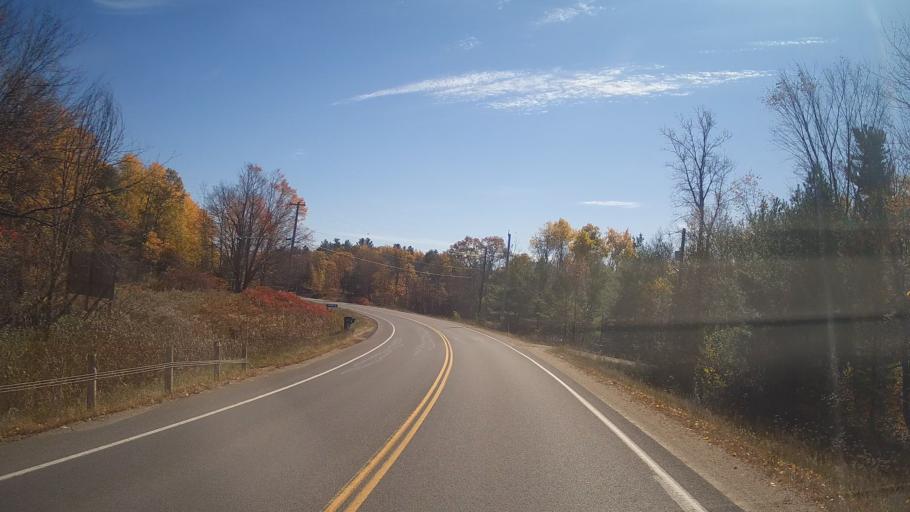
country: CA
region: Ontario
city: Perth
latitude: 44.7274
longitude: -76.6793
